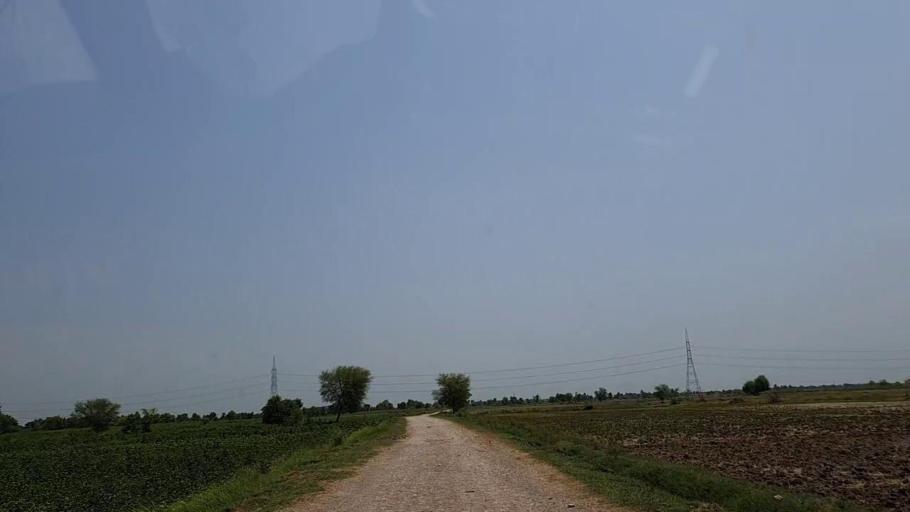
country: PK
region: Sindh
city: Ghotki
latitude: 27.9980
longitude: 69.4100
